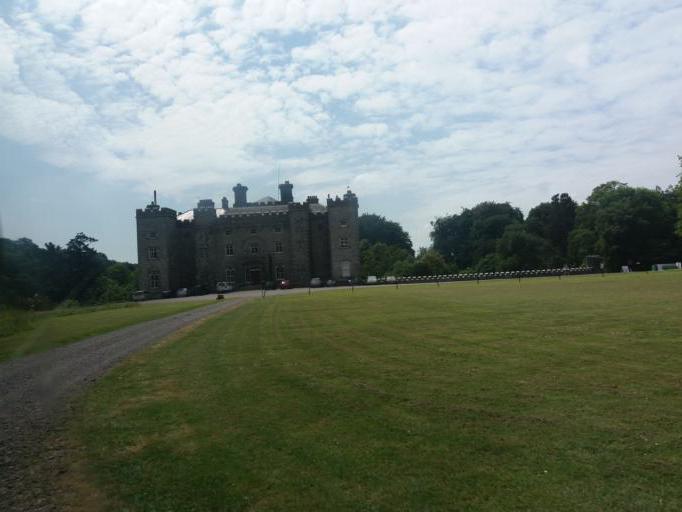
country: IE
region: Leinster
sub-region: An Mhi
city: Slane
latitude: 53.7104
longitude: -6.5606
